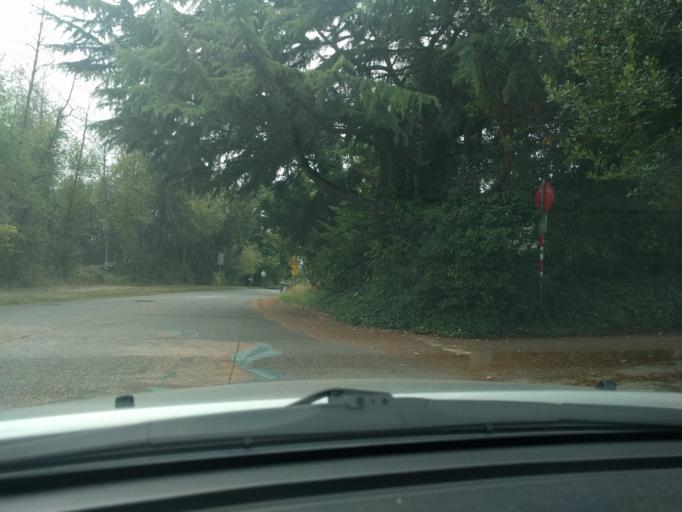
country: US
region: Washington
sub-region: King County
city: White Center
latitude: 47.5649
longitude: -122.3603
